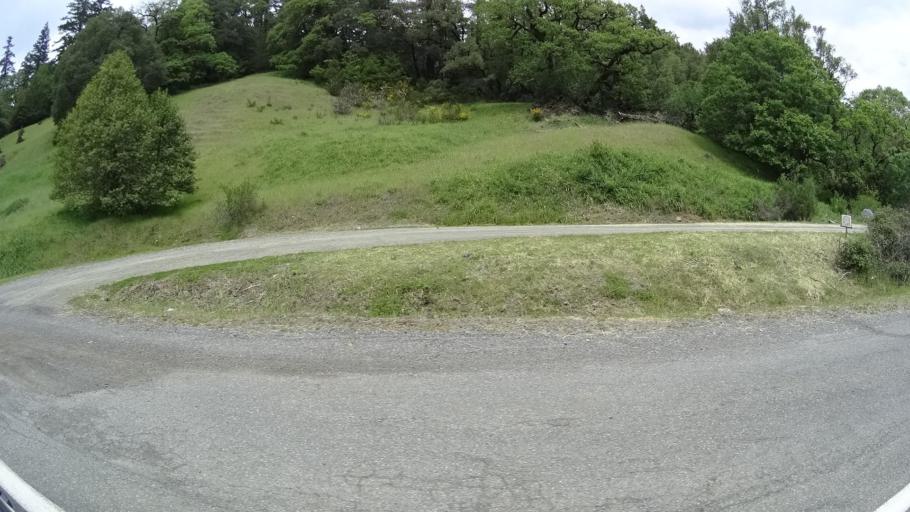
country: US
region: California
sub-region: Humboldt County
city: Redway
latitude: 40.1247
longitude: -123.8737
